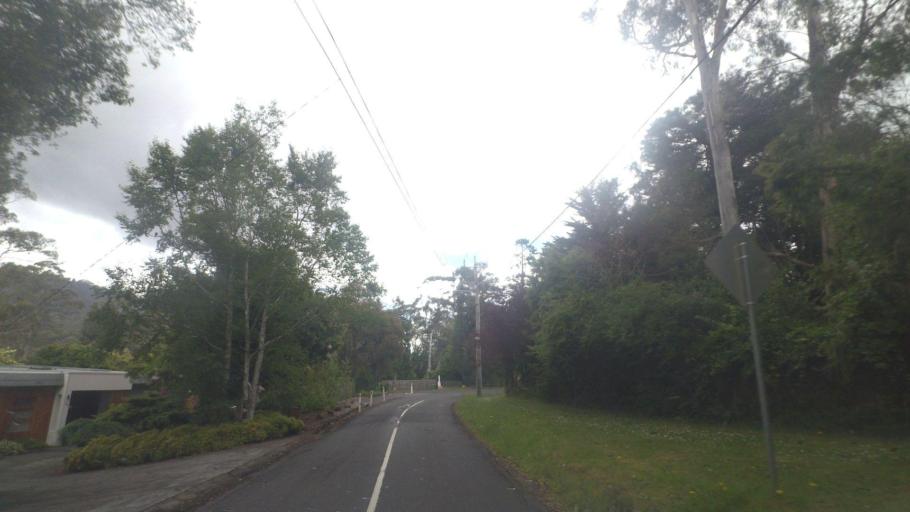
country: AU
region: Victoria
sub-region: Yarra Ranges
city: Mount Evelyn
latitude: -37.7932
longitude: 145.3634
